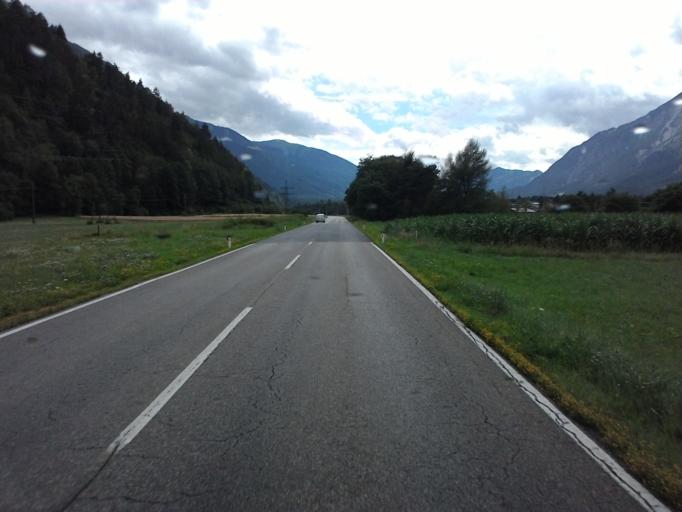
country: AT
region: Tyrol
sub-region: Politischer Bezirk Imst
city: Haiming
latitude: 47.2526
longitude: 10.8907
